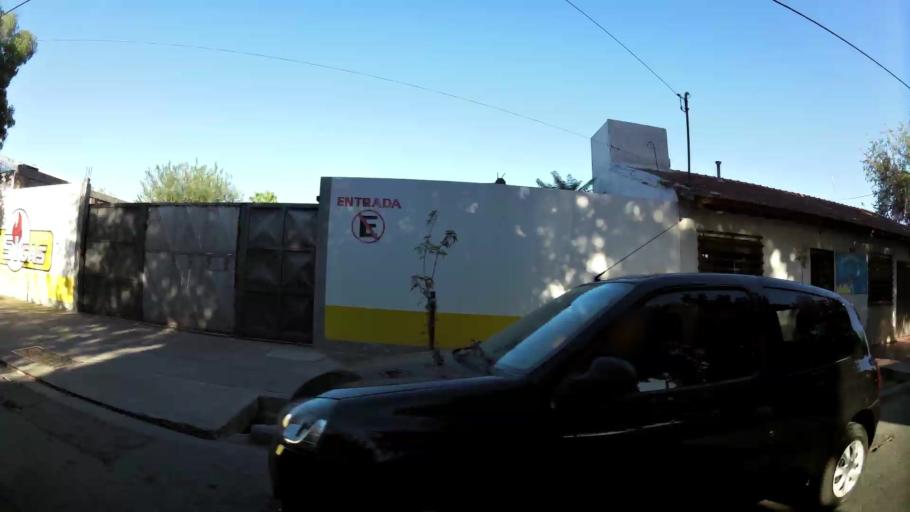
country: AR
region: Mendoza
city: Mendoza
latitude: -32.8734
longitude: -68.8293
